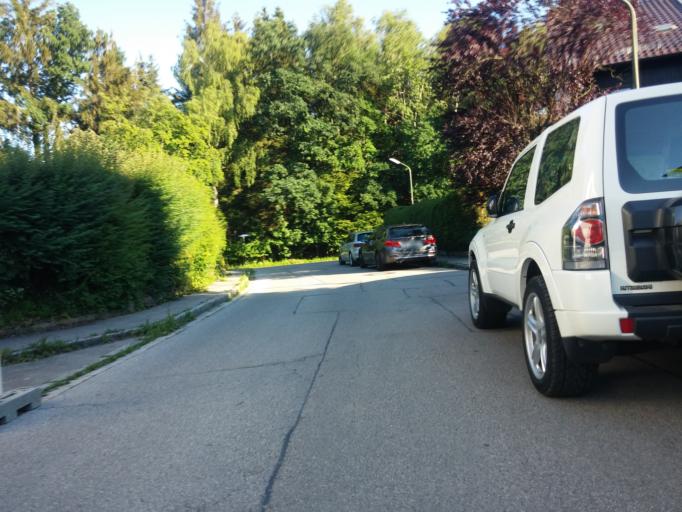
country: DE
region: Bavaria
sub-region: Upper Bavaria
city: Zorneding
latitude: 48.0983
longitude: 11.8058
